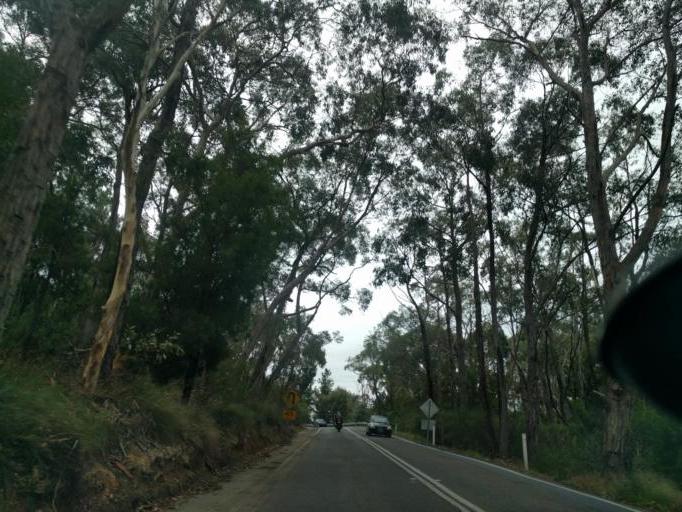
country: AU
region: South Australia
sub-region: Adelaide Hills
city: Bridgewater
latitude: -35.0263
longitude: 138.7656
